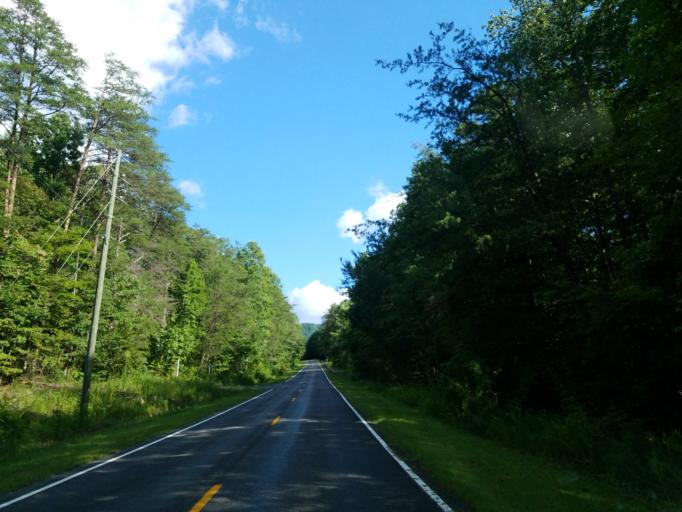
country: US
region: Georgia
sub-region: Fannin County
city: Blue Ridge
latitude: 34.6761
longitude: -84.2858
